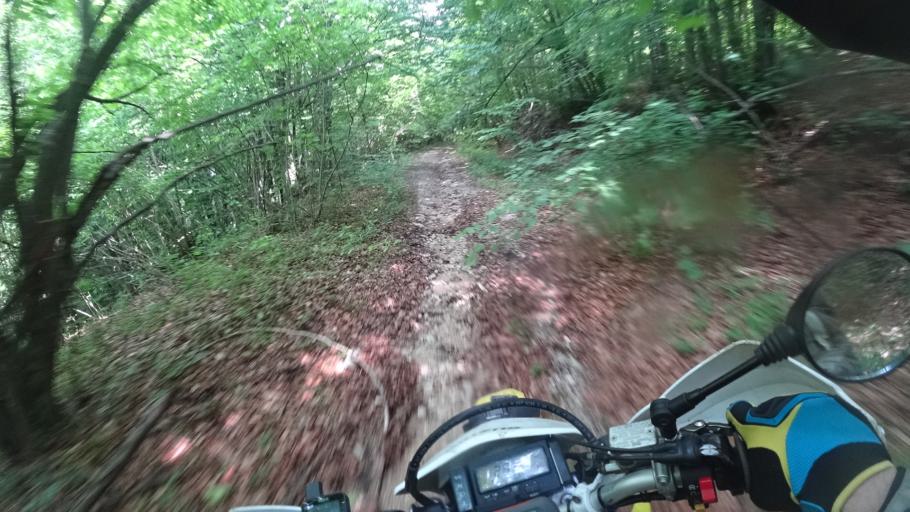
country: BA
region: Federation of Bosnia and Herzegovina
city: Izacic
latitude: 44.8739
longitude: 15.7026
